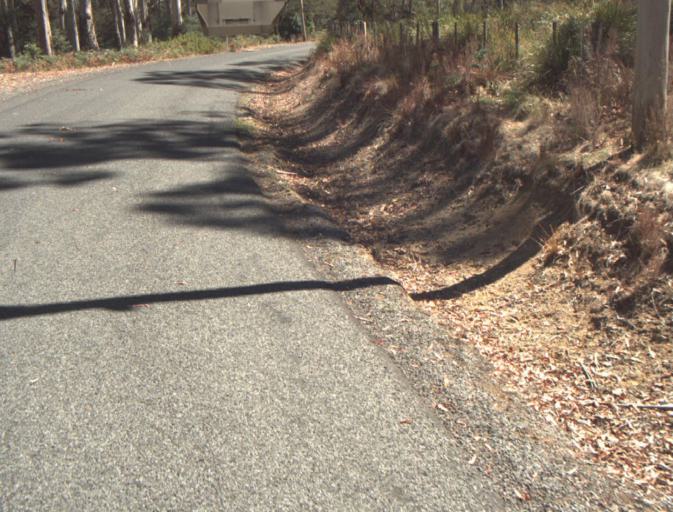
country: AU
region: Tasmania
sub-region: Launceston
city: Newstead
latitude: -41.3617
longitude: 147.3023
